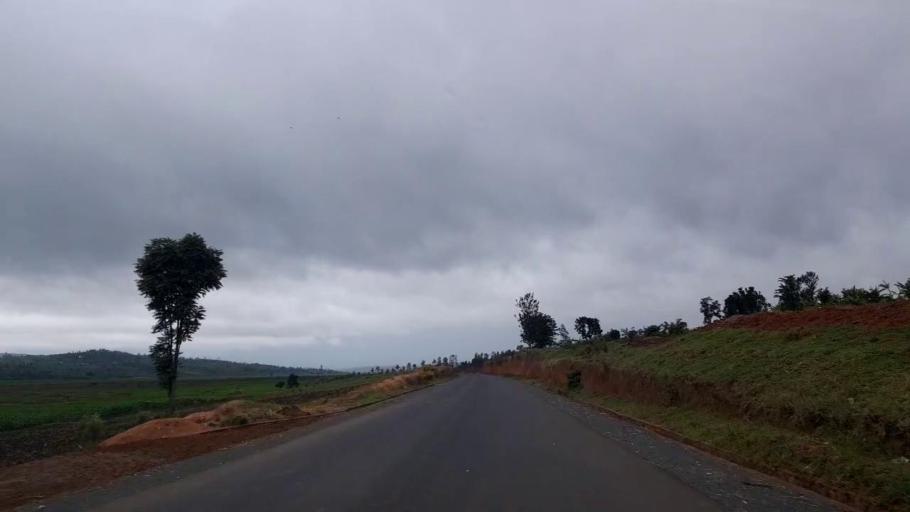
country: RW
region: Northern Province
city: Byumba
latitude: -1.4367
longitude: 30.2581
